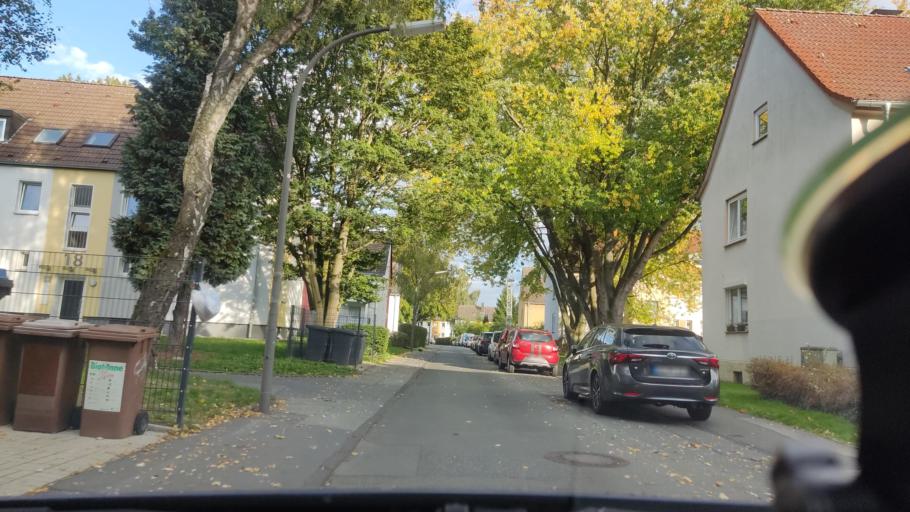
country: DE
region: North Rhine-Westphalia
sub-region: Regierungsbezirk Arnsberg
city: Dortmund
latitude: 51.5572
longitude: 7.4770
